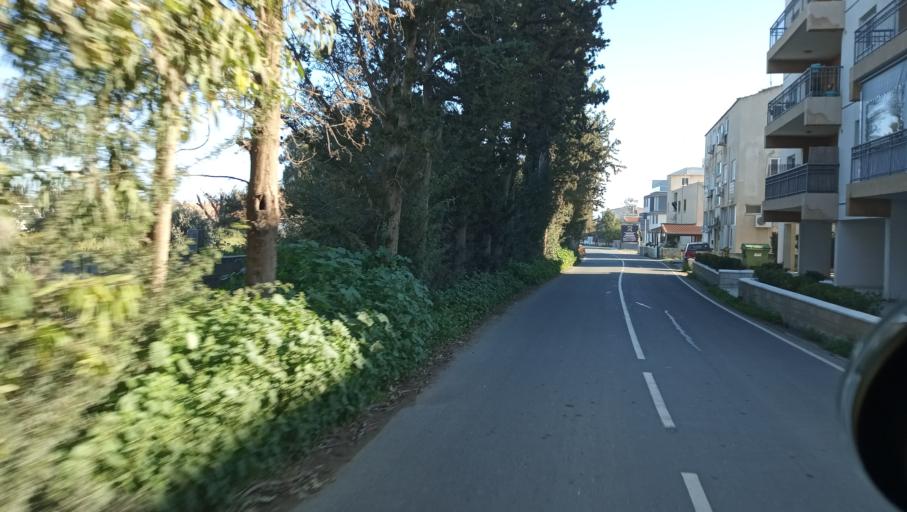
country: CY
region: Lefkosia
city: Nicosia
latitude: 35.1326
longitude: 33.3264
